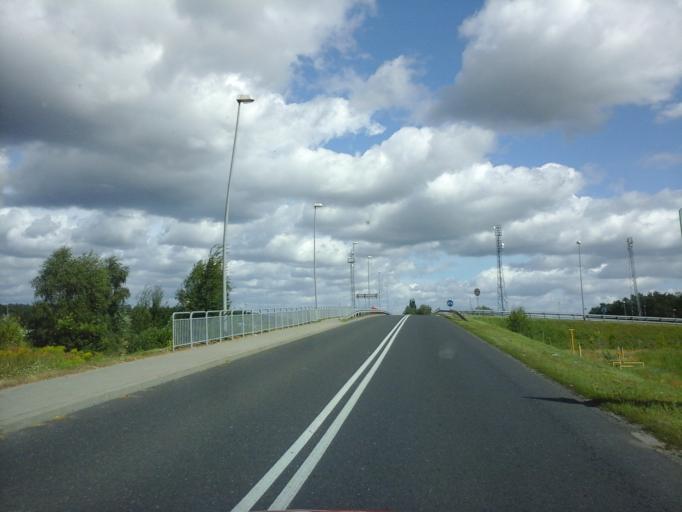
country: PL
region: West Pomeranian Voivodeship
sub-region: Powiat stargardzki
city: Kobylanka
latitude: 53.3477
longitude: 14.8486
